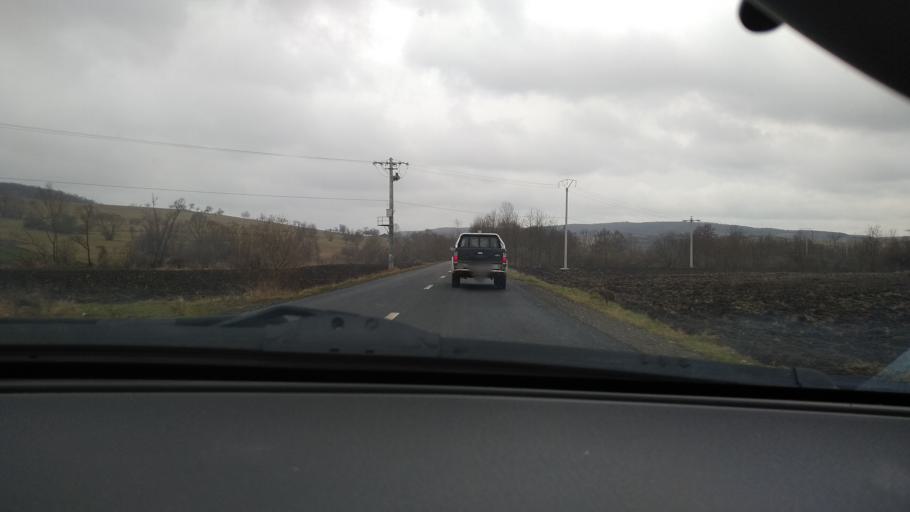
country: RO
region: Mures
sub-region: Comuna Magherani
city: Magherani
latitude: 46.5586
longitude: 24.8898
